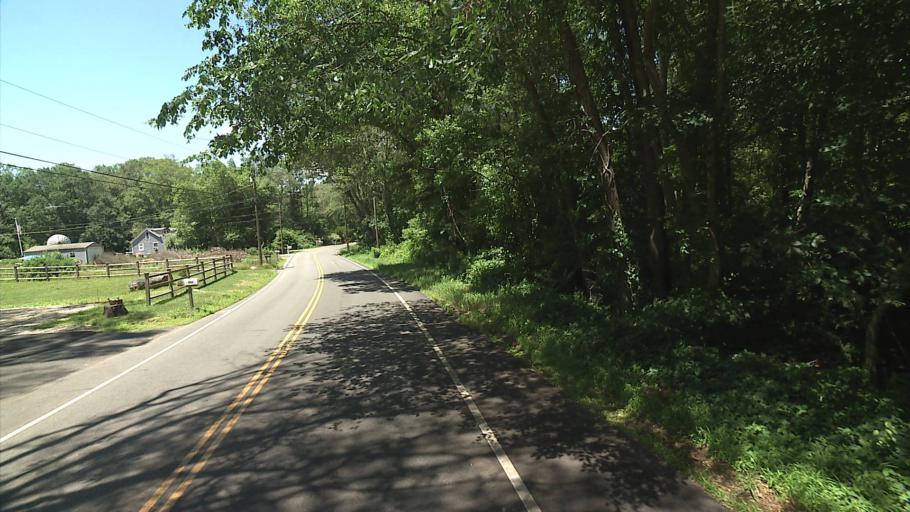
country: US
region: Connecticut
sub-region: New London County
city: Old Mystic
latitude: 41.3760
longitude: -71.9200
